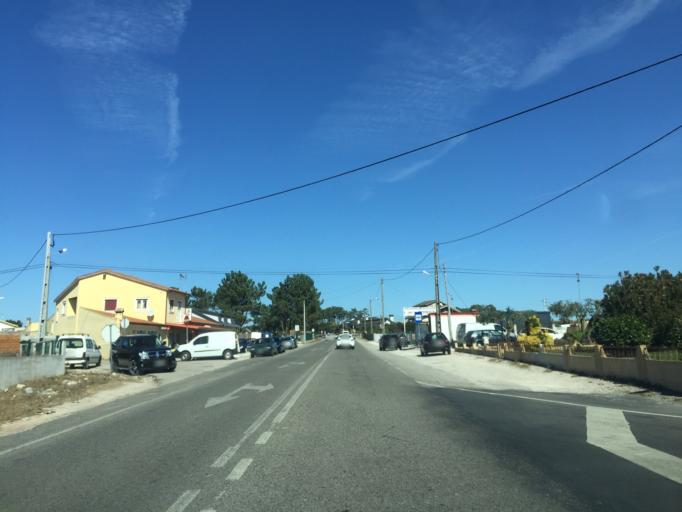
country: PT
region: Coimbra
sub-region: Figueira da Foz
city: Alhadas
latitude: 40.2555
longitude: -8.7810
